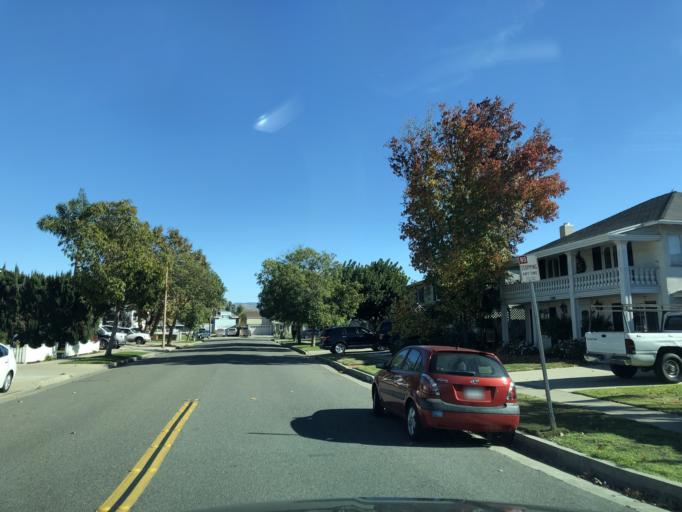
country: US
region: California
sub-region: Orange County
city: Tustin
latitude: 33.7657
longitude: -117.8332
